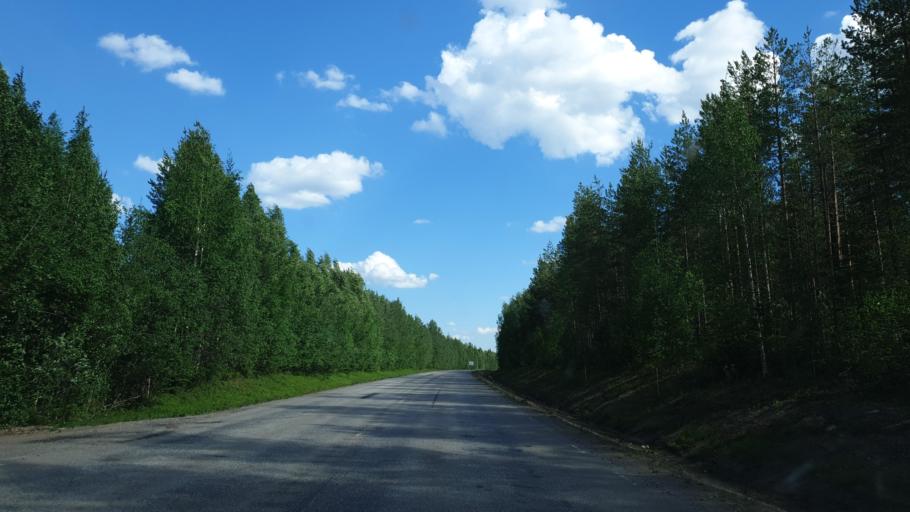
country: SE
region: Norrbotten
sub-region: Alvsbyns Kommun
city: AElvsbyn
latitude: 65.8317
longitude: 20.5413
